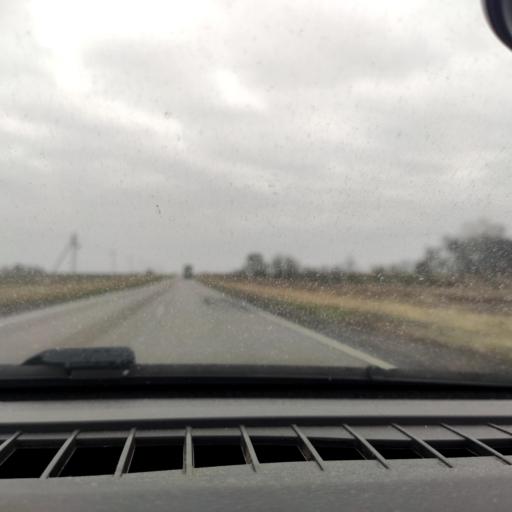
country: RU
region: Belgorod
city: Ilovka
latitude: 50.7690
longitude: 38.7594
